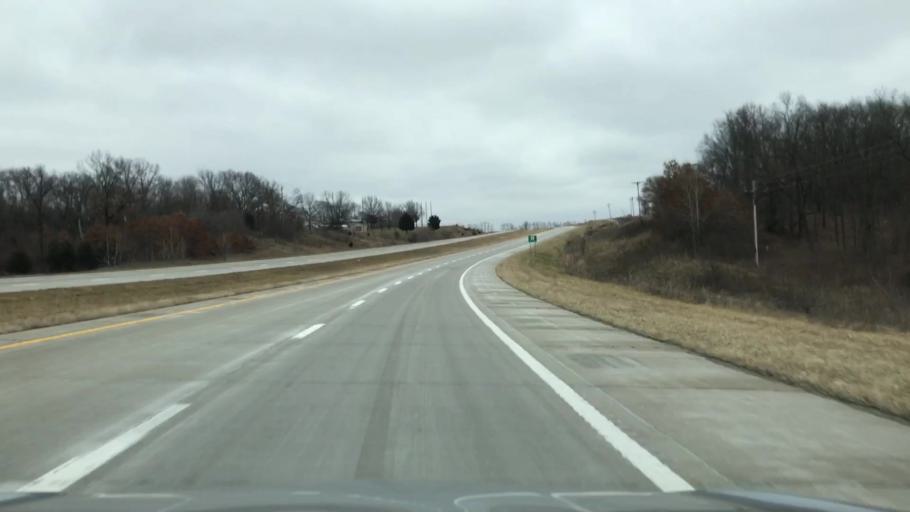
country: US
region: Missouri
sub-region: Livingston County
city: Chillicothe
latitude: 39.7395
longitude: -93.6391
